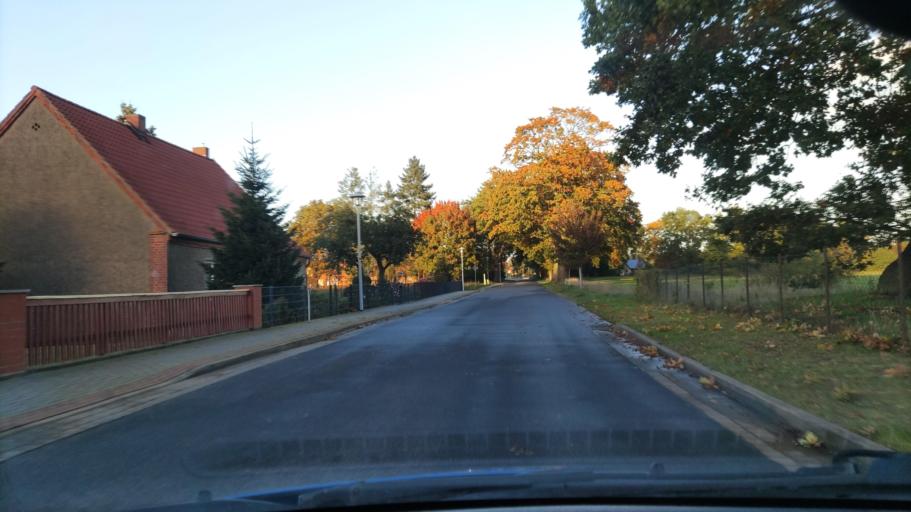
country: DE
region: Mecklenburg-Vorpommern
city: Lubtheen
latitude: 53.3134
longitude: 11.0042
